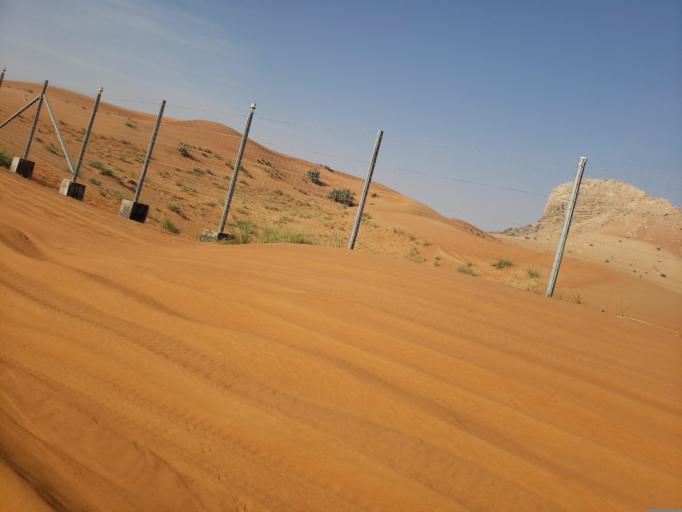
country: AE
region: Ash Shariqah
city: Adh Dhayd
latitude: 25.1402
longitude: 55.8417
